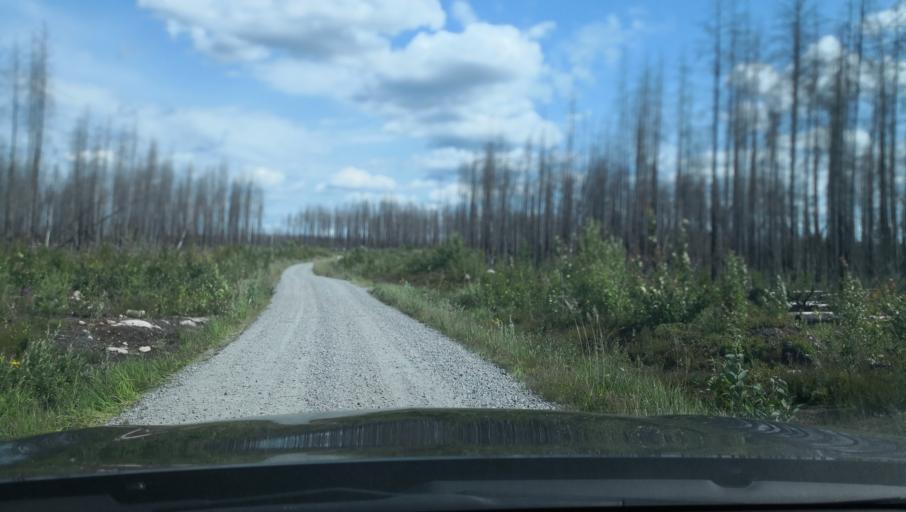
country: SE
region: Vaestmanland
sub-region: Surahammars Kommun
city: Ramnas
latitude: 59.8974
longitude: 16.1204
